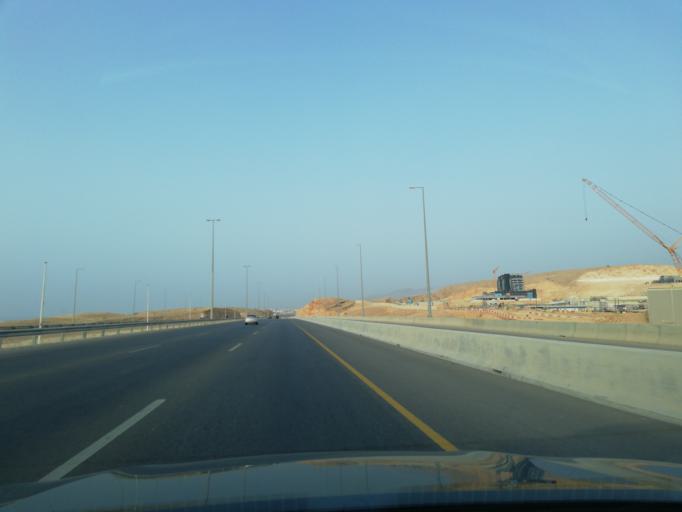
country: OM
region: Muhafazat Masqat
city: Bawshar
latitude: 23.5529
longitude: 58.2956
